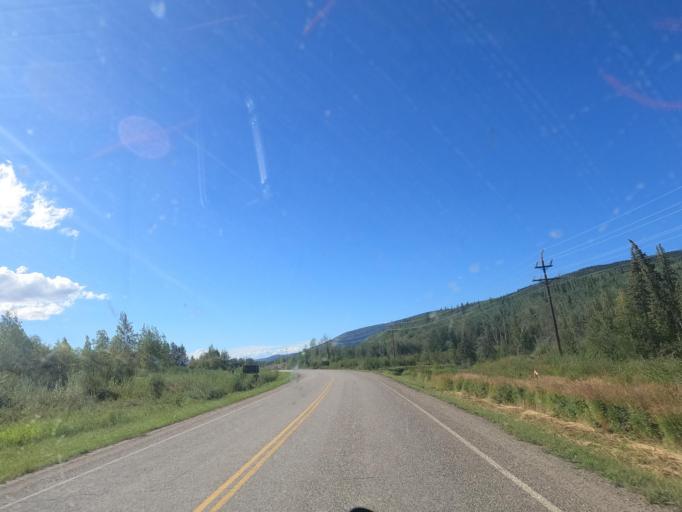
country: CA
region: Yukon
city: Dawson City
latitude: 64.0328
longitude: -139.1952
